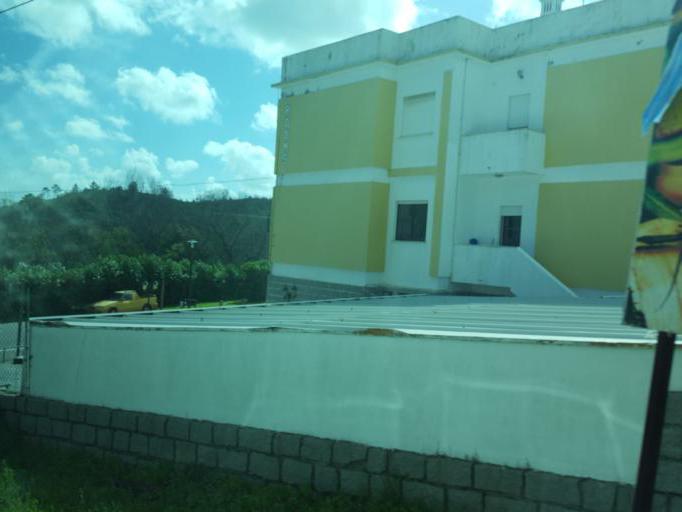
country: PT
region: Faro
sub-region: Monchique
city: Monchique
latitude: 37.2800
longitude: -8.5546
